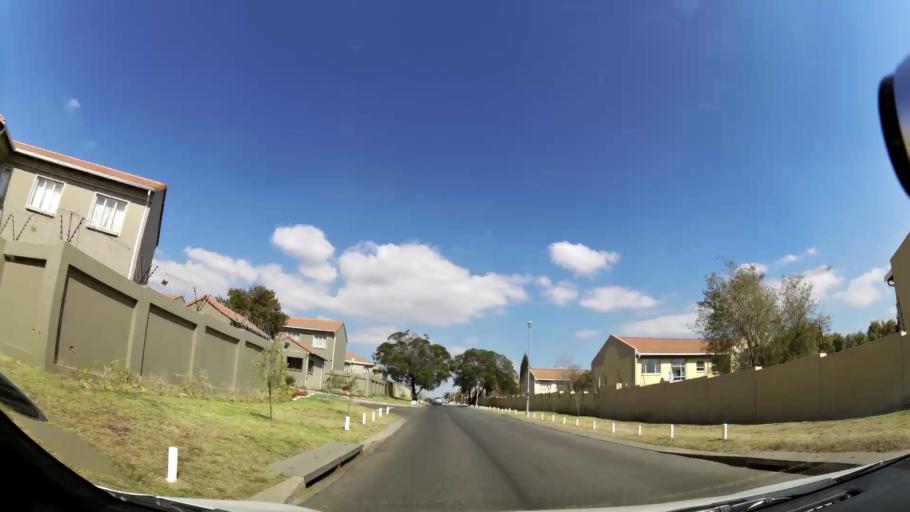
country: ZA
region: Gauteng
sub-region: City of Johannesburg Metropolitan Municipality
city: Midrand
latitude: -26.0052
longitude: 28.1105
